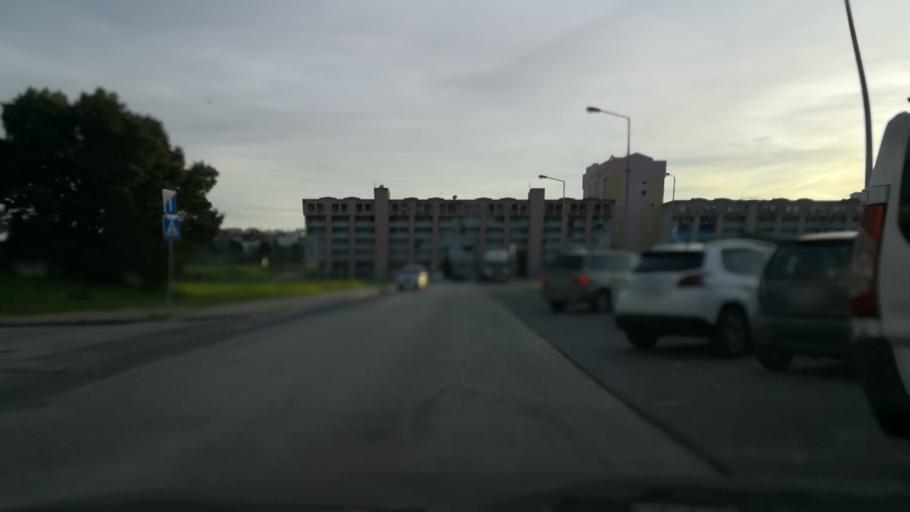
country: PT
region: Setubal
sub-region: Setubal
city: Setubal
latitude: 38.5323
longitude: -8.8653
